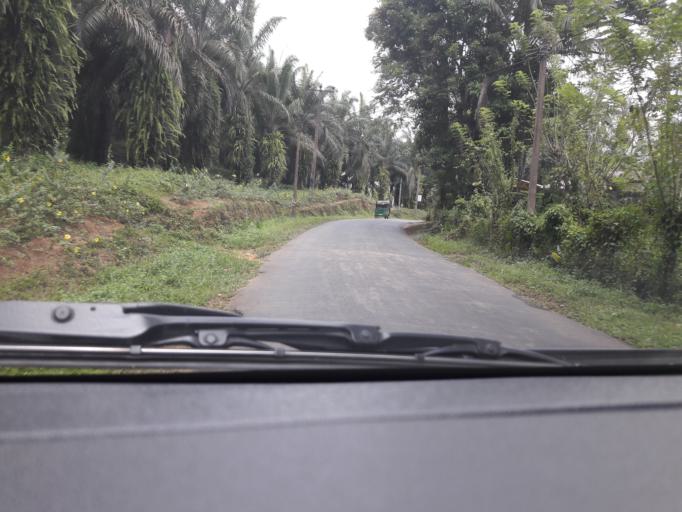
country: LK
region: Southern
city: Hikkaduwa
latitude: 6.2582
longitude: 80.2647
